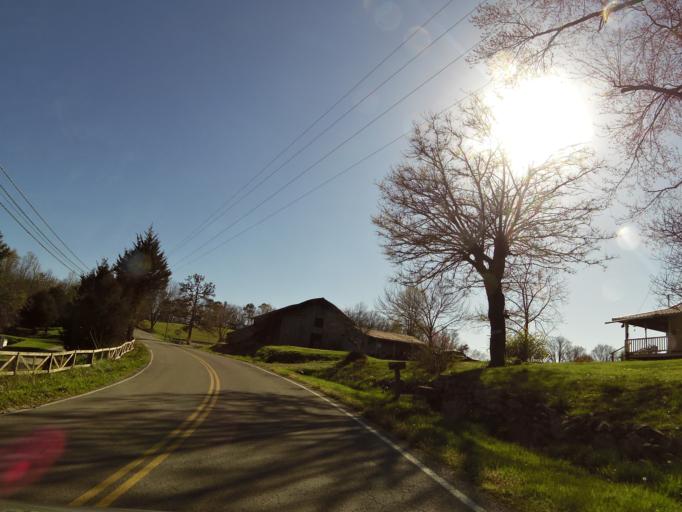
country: US
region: Tennessee
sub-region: Scott County
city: Huntsville
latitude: 36.3637
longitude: -84.3972
